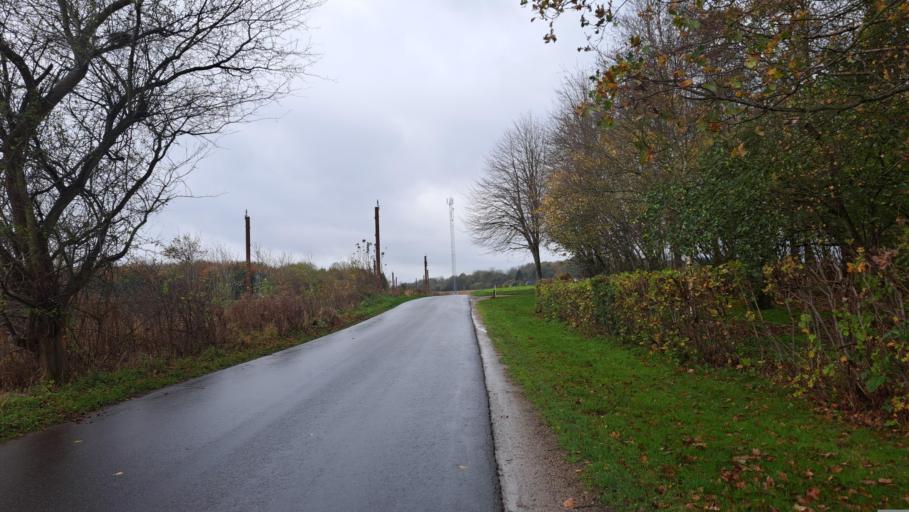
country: DK
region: Central Jutland
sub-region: Hedensted Kommune
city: Hedensted
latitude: 55.8152
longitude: 9.7105
